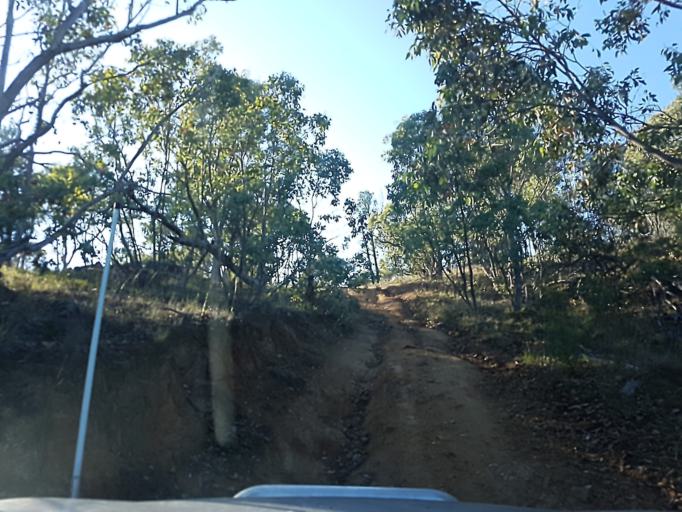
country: AU
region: New South Wales
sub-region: Snowy River
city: Jindabyne
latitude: -36.9577
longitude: 148.3764
